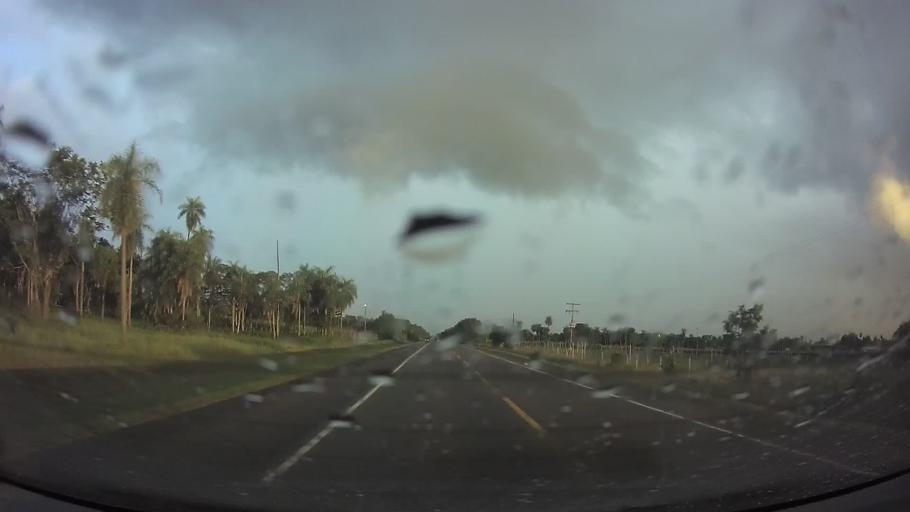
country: PY
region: Paraguari
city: Paraguari
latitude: -25.6142
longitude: -57.1805
